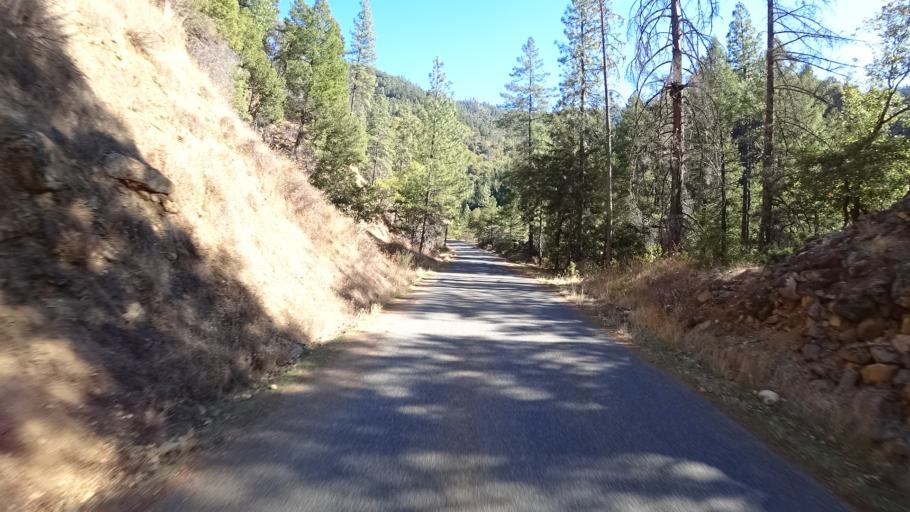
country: US
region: California
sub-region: Humboldt County
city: Willow Creek
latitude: 41.2823
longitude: -123.2596
